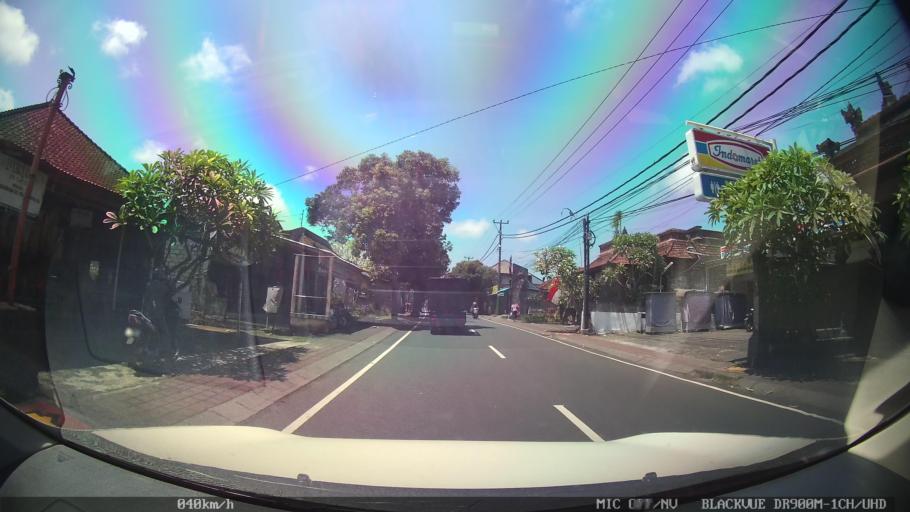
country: ID
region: Bali
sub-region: Kabupaten Gianyar
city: Ubud
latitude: -8.5585
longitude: 115.3117
